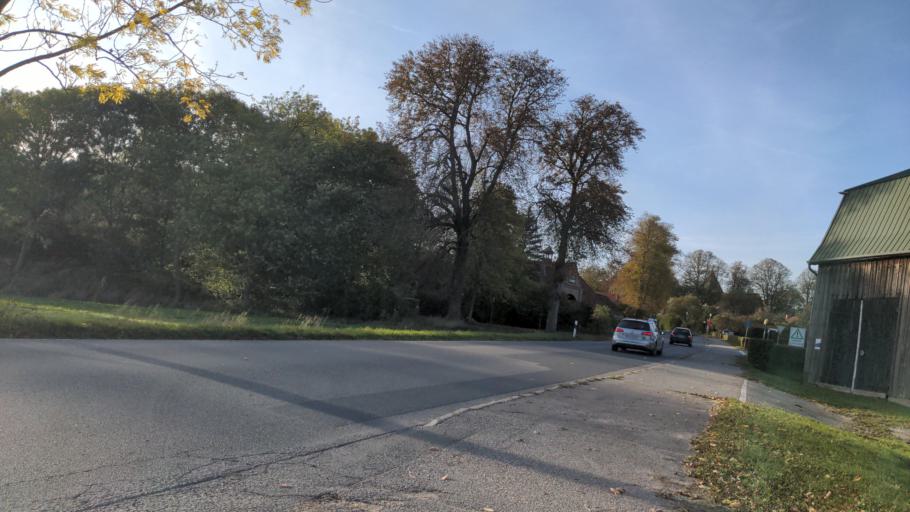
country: DE
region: Schleswig-Holstein
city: Kirchnuchel
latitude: 54.2033
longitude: 10.6819
